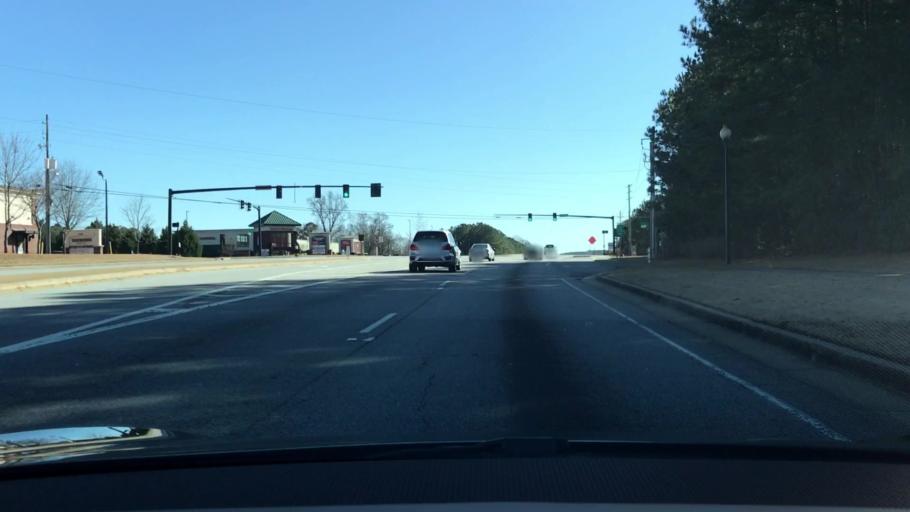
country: US
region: Georgia
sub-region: Gwinnett County
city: Suwanee
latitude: 34.0452
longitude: -84.0853
